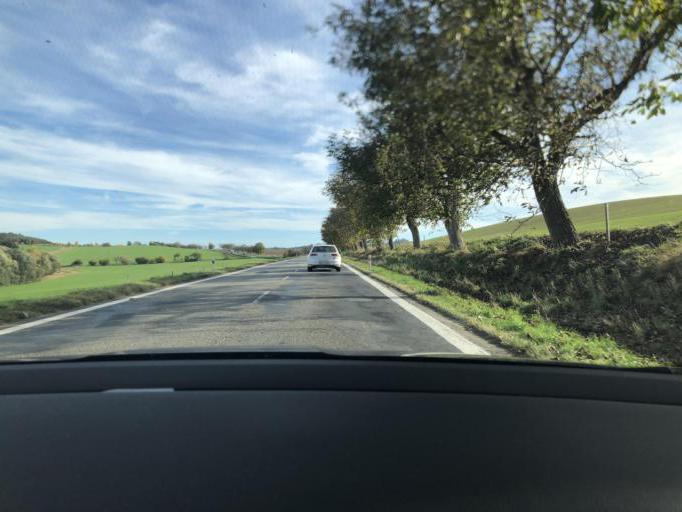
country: CZ
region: Central Bohemia
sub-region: Okres Benesov
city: Benesov
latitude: 49.7759
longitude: 14.7218
